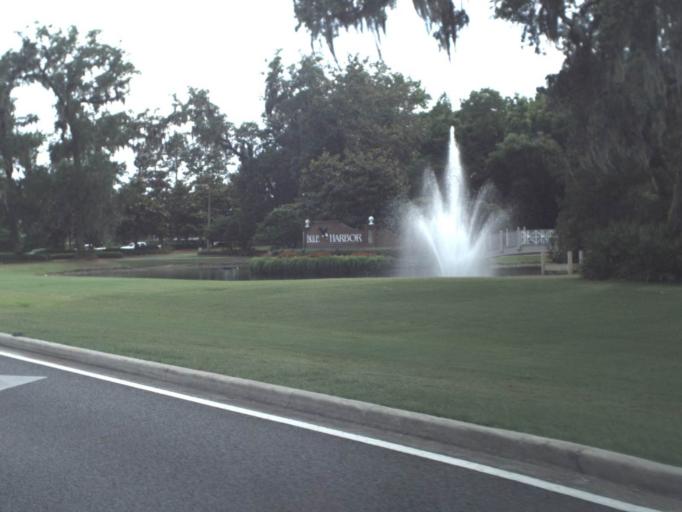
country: US
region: Florida
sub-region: Clay County
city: Orange Park
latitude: 30.1068
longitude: -81.7055
